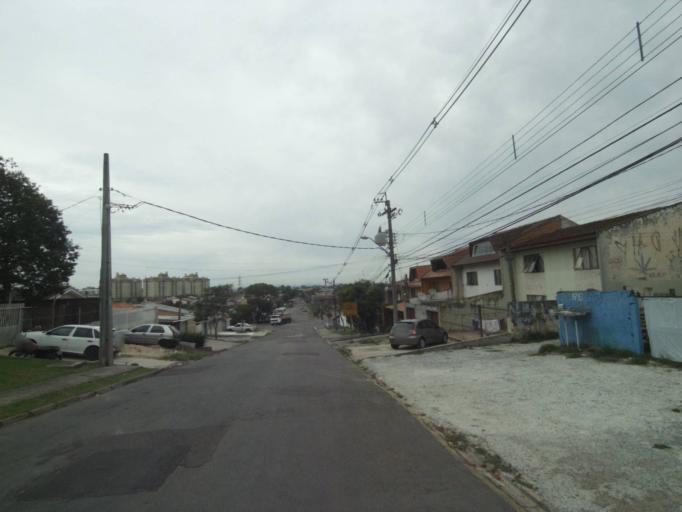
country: BR
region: Parana
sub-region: Pinhais
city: Pinhais
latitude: -25.4268
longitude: -49.2048
